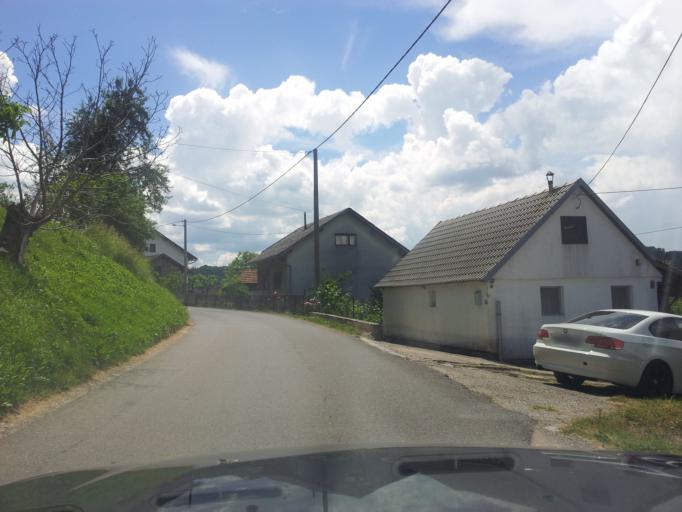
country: HR
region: Karlovacka
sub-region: Grad Karlovac
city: Karlovac
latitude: 45.4592
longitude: 15.4982
